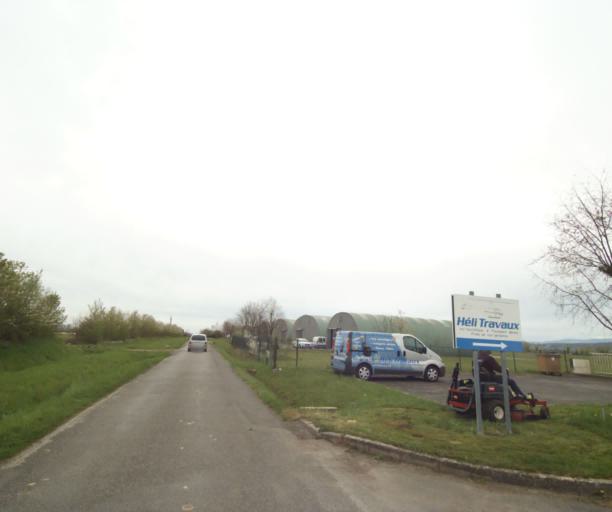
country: FR
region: Bourgogne
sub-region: Departement de Saone-et-Loire
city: Charnay-les-Macon
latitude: 46.2941
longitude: 4.7992
